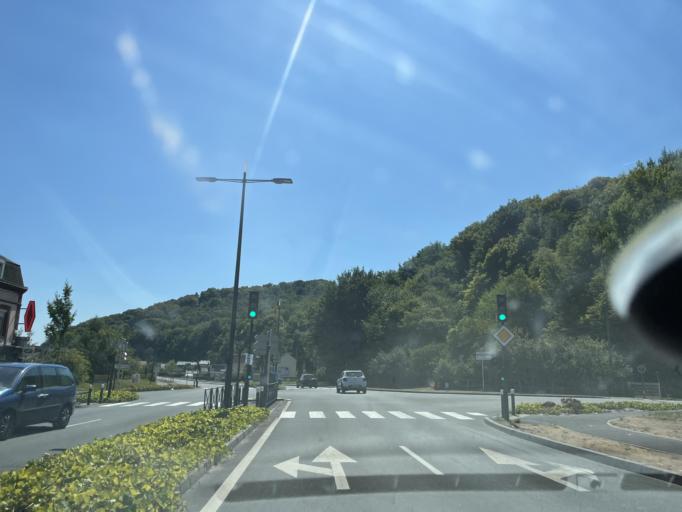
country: FR
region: Haute-Normandie
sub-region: Departement de la Seine-Maritime
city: Lillebonne
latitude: 49.5202
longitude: 0.5286
